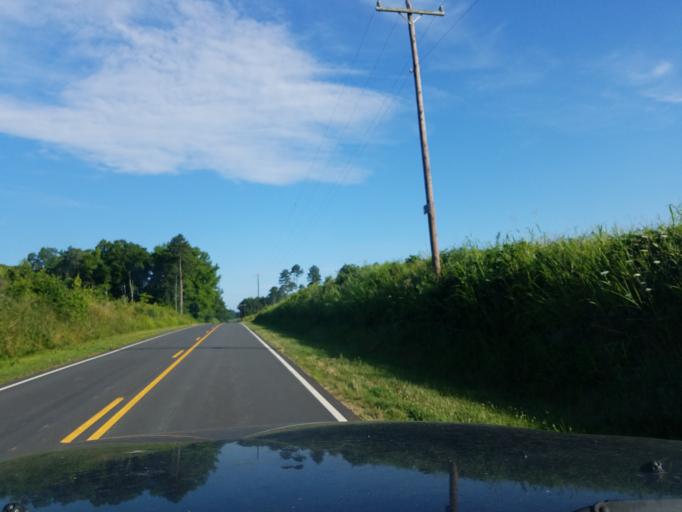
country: US
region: North Carolina
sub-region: Granville County
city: Butner
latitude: 36.1676
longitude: -78.7866
